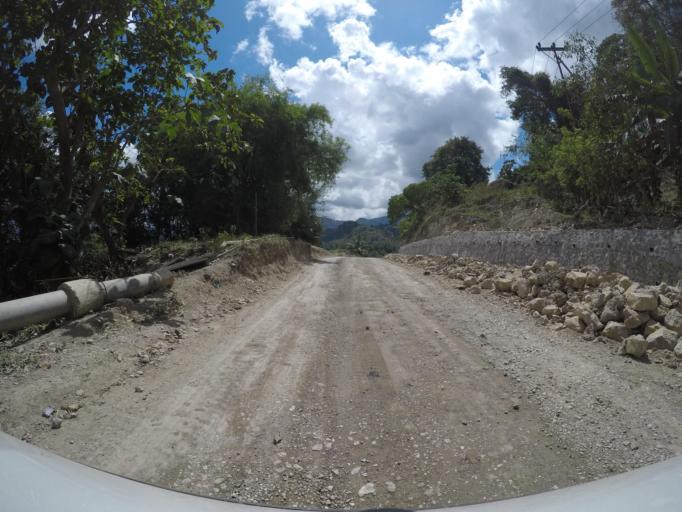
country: TL
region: Viqueque
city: Viqueque
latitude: -8.8291
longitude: 126.3745
